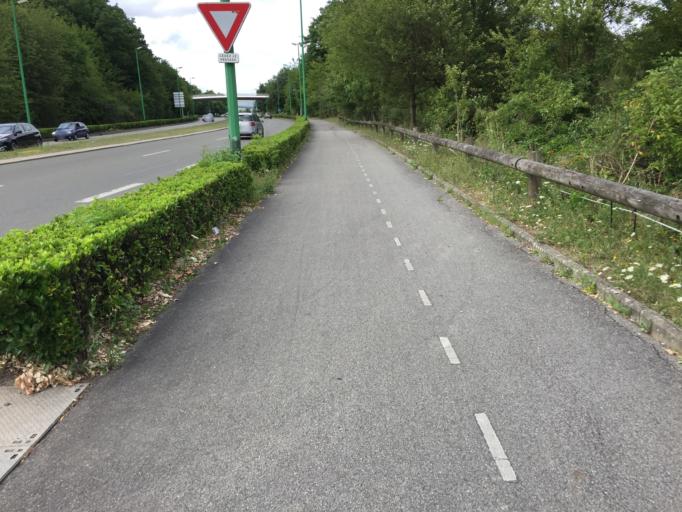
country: FR
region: Ile-de-France
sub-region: Departement des Yvelines
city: Guyancourt
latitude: 48.7779
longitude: 2.0606
